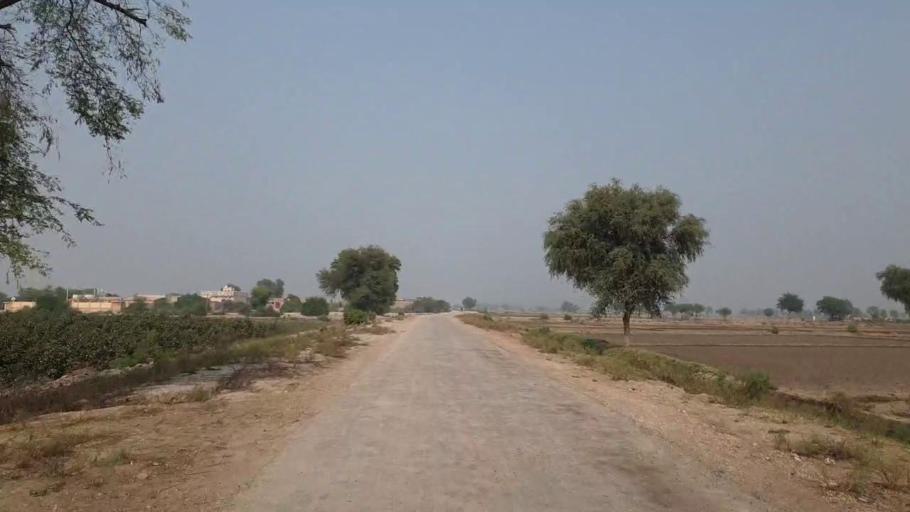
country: PK
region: Sindh
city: Bhan
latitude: 26.5124
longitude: 67.6895
